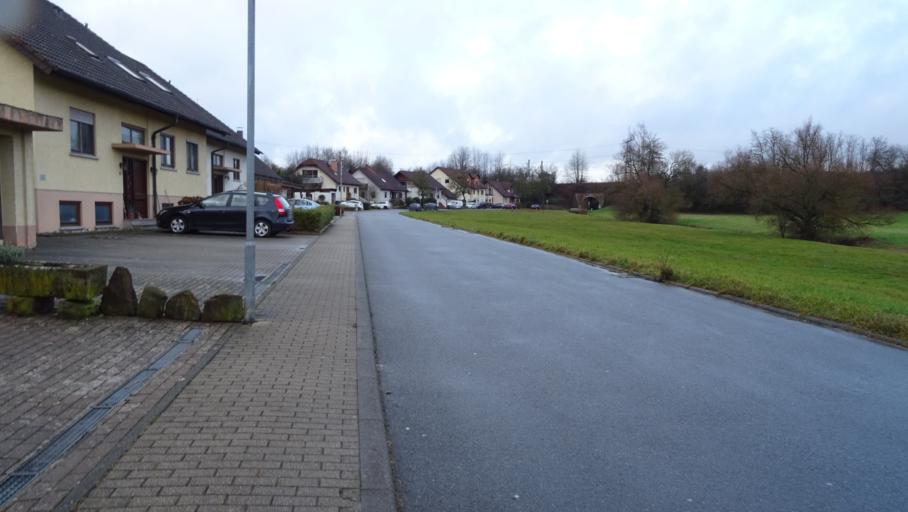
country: DE
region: Baden-Wuerttemberg
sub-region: Karlsruhe Region
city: Seckach
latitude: 49.4145
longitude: 9.2766
